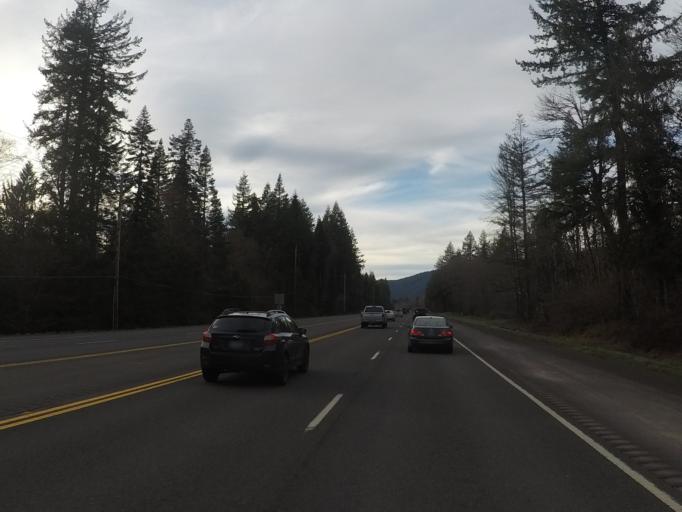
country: US
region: Oregon
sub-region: Clackamas County
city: Mount Hood Village
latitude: 45.3628
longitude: -122.0007
